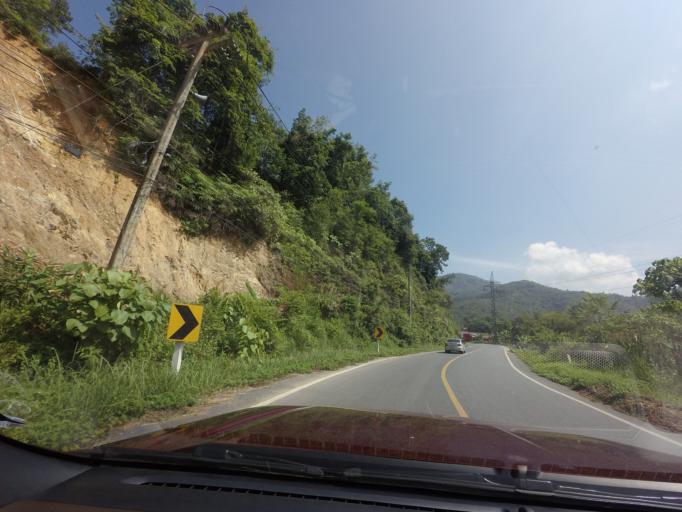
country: TH
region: Yala
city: Betong
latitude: 5.9173
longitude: 101.1691
